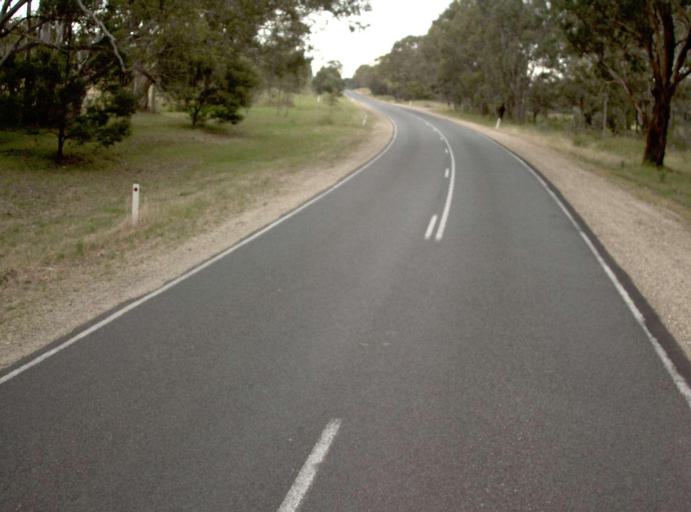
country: AU
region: Victoria
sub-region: Wellington
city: Sale
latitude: -38.1776
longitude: 147.1476
